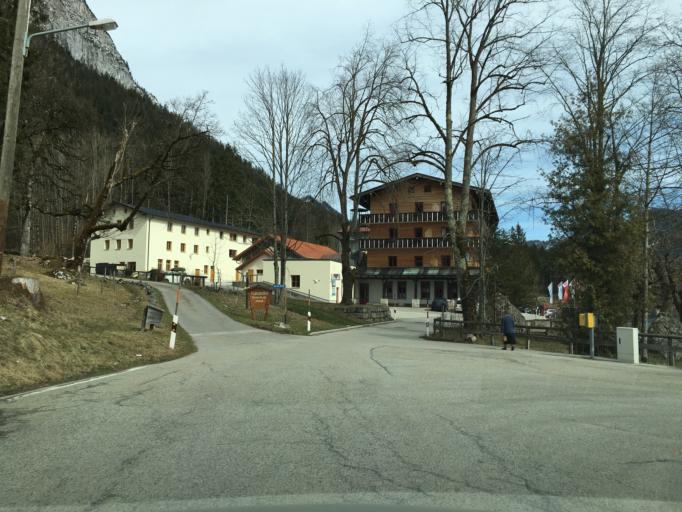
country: DE
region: Bavaria
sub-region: Upper Bavaria
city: Ramsau
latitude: 47.6065
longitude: 12.8506
